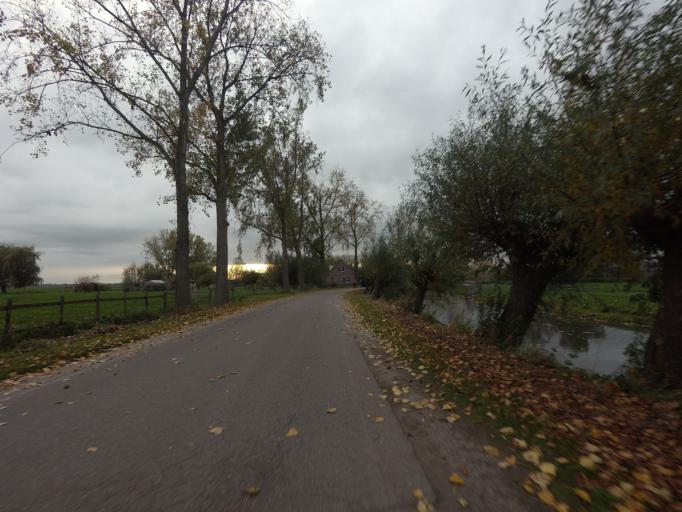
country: NL
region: Utrecht
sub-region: Gemeente Montfoort
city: Montfoort
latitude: 52.0764
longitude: 4.9804
